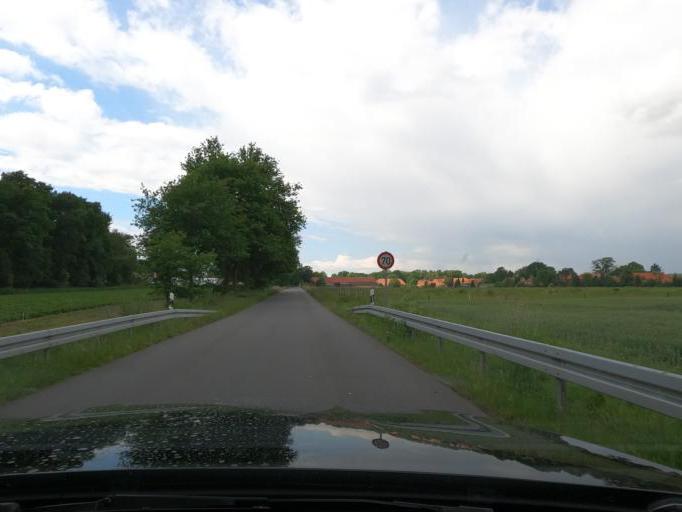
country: DE
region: Lower Saxony
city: Steimbke
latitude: 52.6433
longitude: 9.4477
